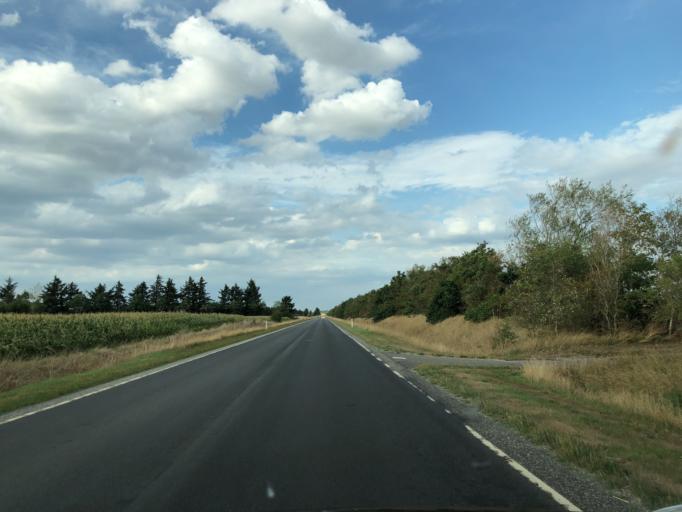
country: DK
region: Central Jutland
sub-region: Holstebro Kommune
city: Holstebro
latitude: 56.3842
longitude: 8.4516
